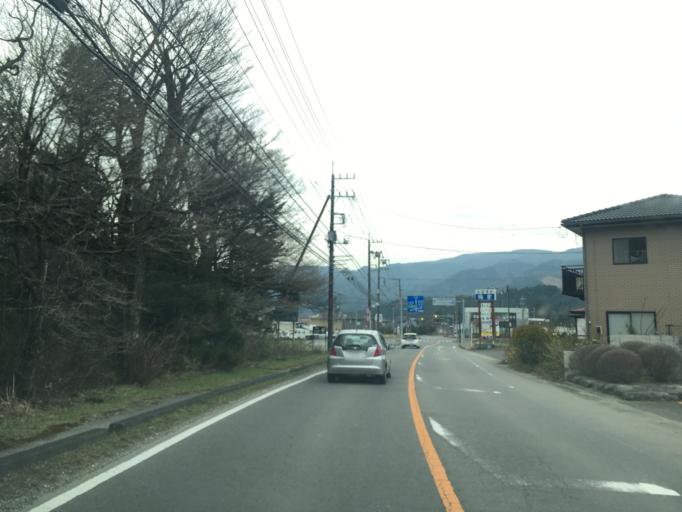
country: JP
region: Tochigi
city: Kuroiso
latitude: 36.9550
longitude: 139.9028
